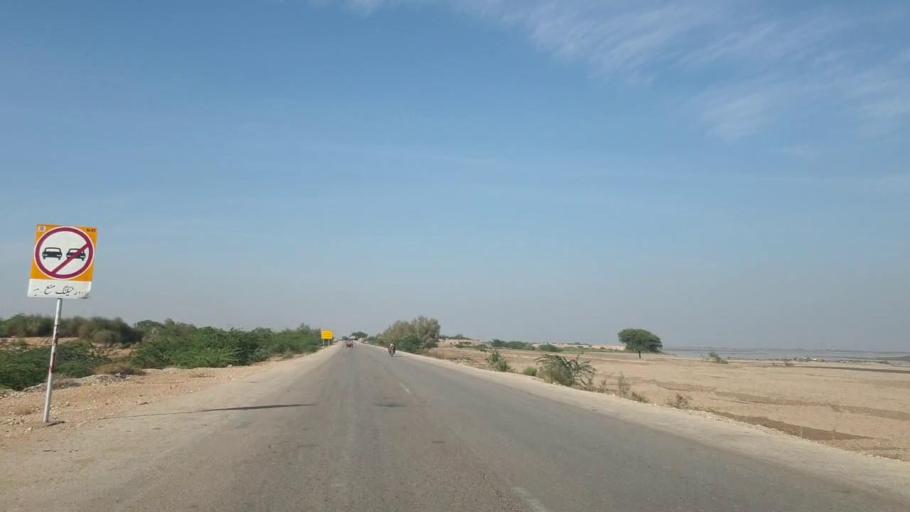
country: PK
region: Sindh
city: Sehwan
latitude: 26.3815
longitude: 67.8719
